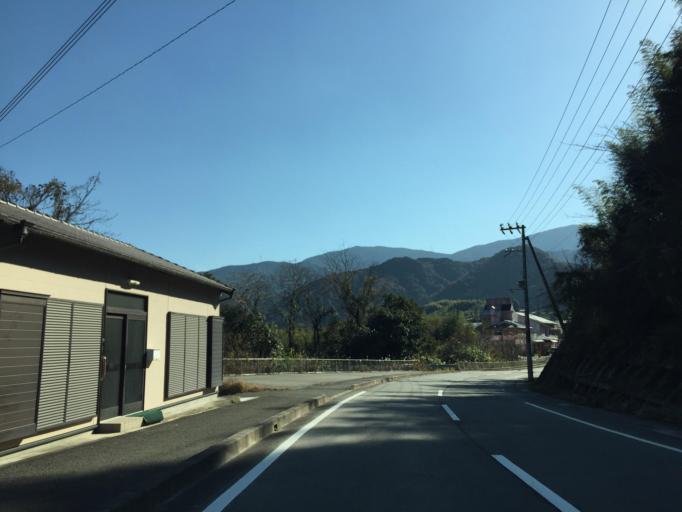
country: JP
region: Wakayama
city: Iwade
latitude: 34.1505
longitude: 135.3458
